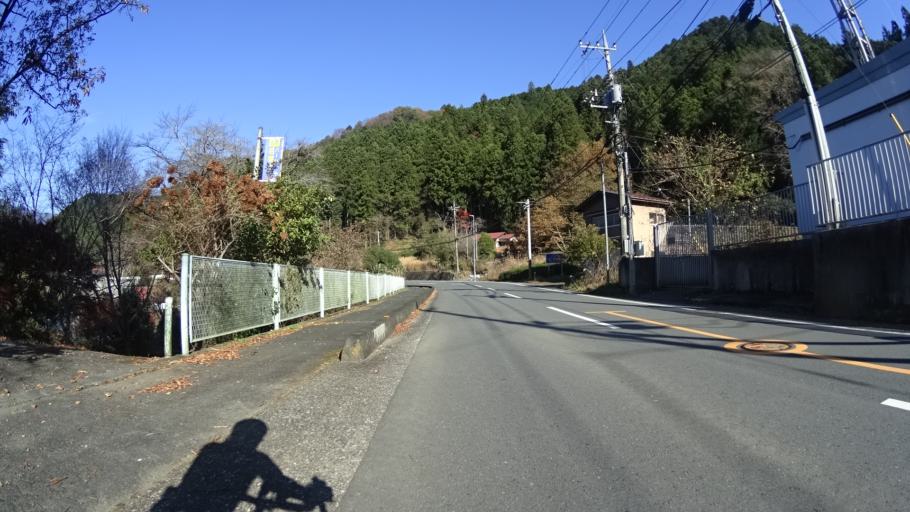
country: JP
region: Tokyo
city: Ome
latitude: 35.8938
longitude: 139.1772
